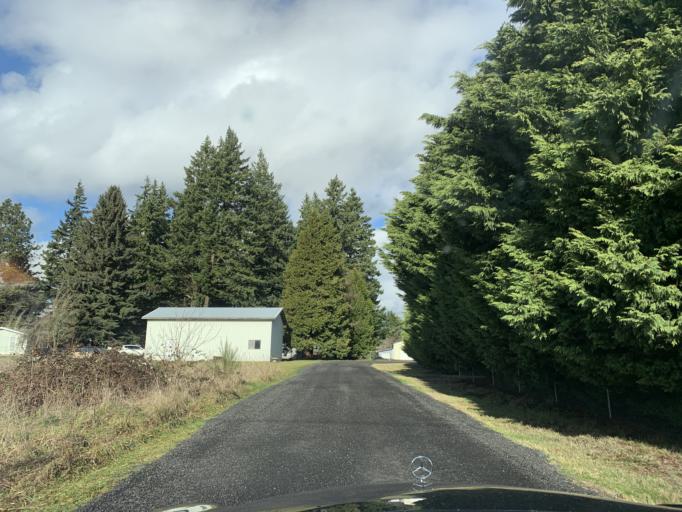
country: US
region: Washington
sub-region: Skamania County
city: Carson
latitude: 45.7231
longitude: -121.8152
